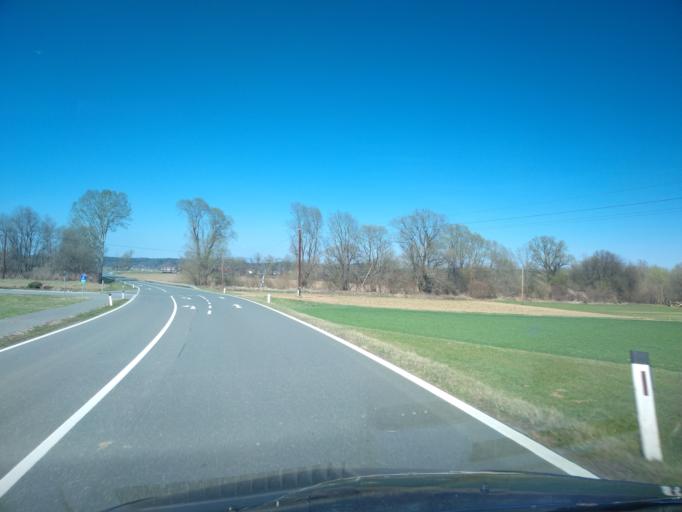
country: AT
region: Styria
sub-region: Politischer Bezirk Deutschlandsberg
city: Preding
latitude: 46.8991
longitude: 15.4080
